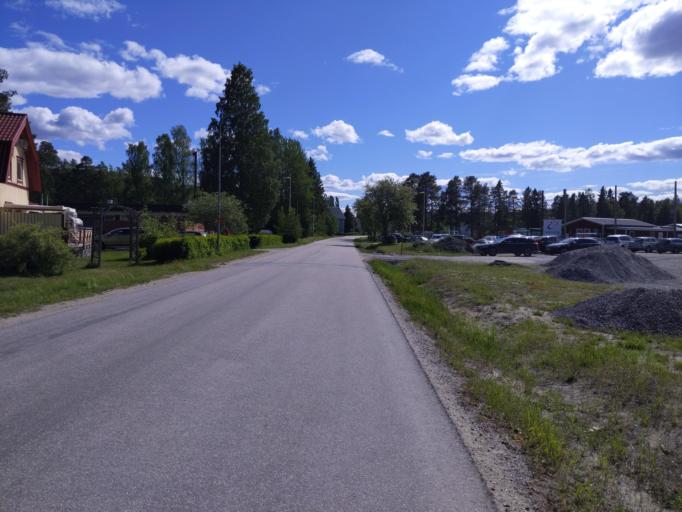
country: SE
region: Vaesternorrland
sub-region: OErnskoeldsviks Kommun
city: Kopmanholmen
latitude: 63.1720
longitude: 18.5671
